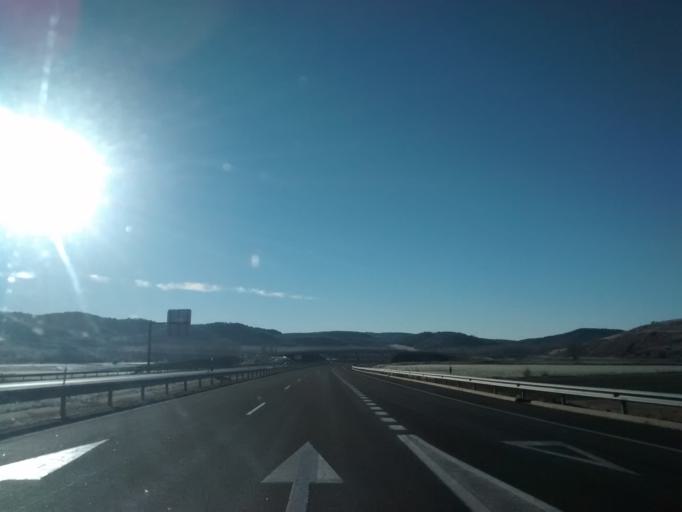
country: ES
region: Castille and Leon
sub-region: Provincia de Palencia
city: Alar del Rey
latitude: 42.7148
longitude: -4.2892
